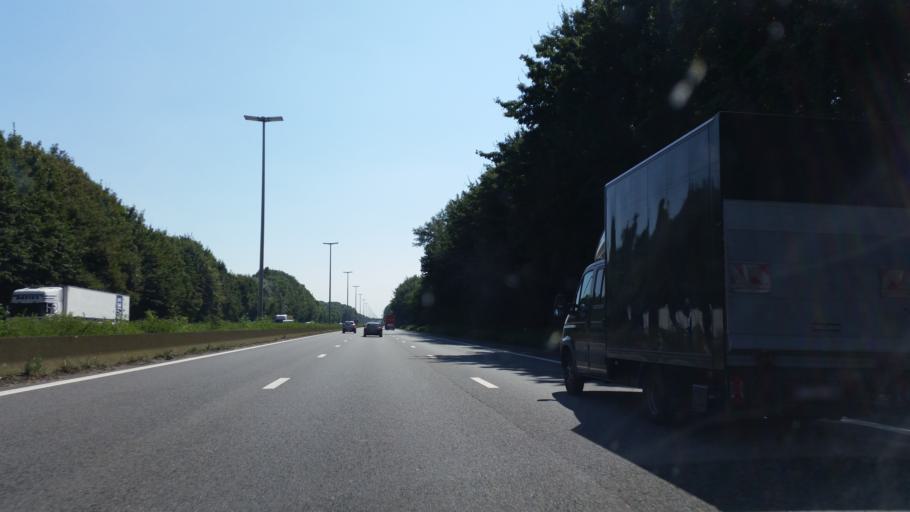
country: BE
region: Wallonia
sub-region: Province du Brabant Wallon
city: Walhain-Saint-Paul
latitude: 50.6302
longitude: 4.7522
